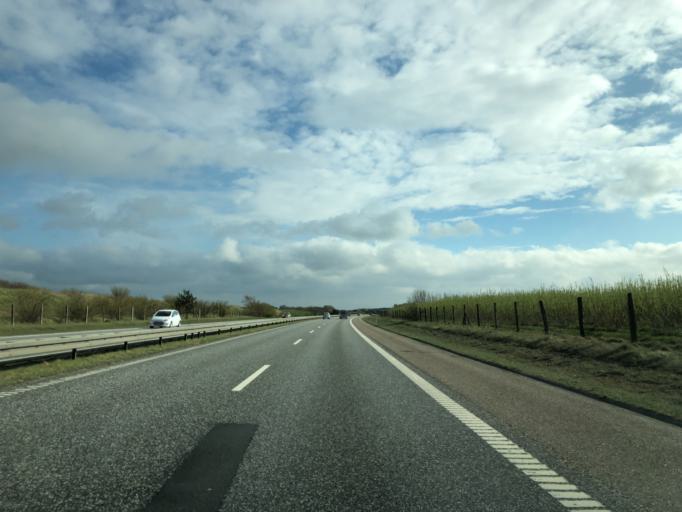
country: DK
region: North Denmark
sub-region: Alborg Kommune
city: Vestbjerg
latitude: 57.1787
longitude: 9.9439
